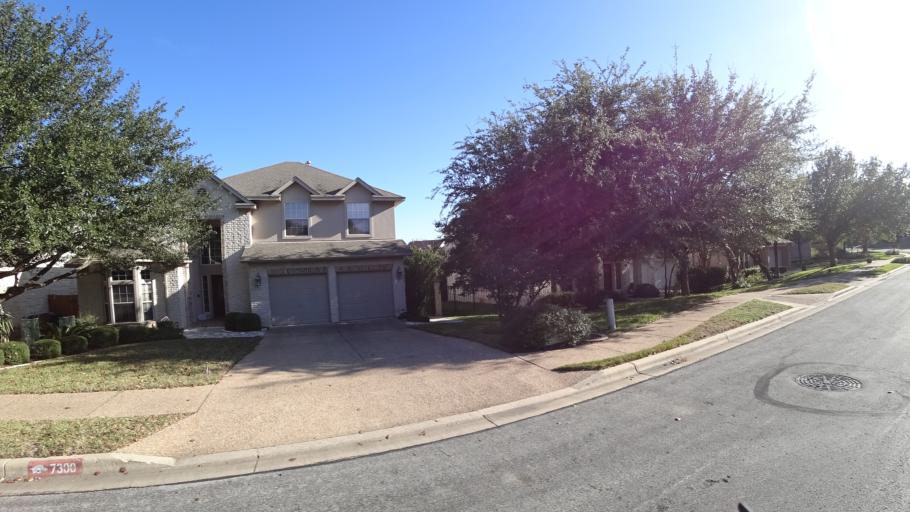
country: US
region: Texas
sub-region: Williamson County
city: Jollyville
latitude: 30.4119
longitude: -97.7753
